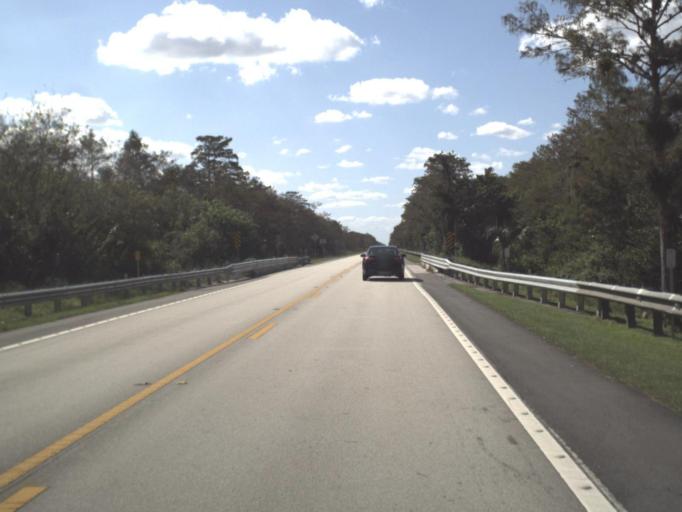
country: US
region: Florida
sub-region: Miami-Dade County
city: Kendall West
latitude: 25.8466
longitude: -80.9316
